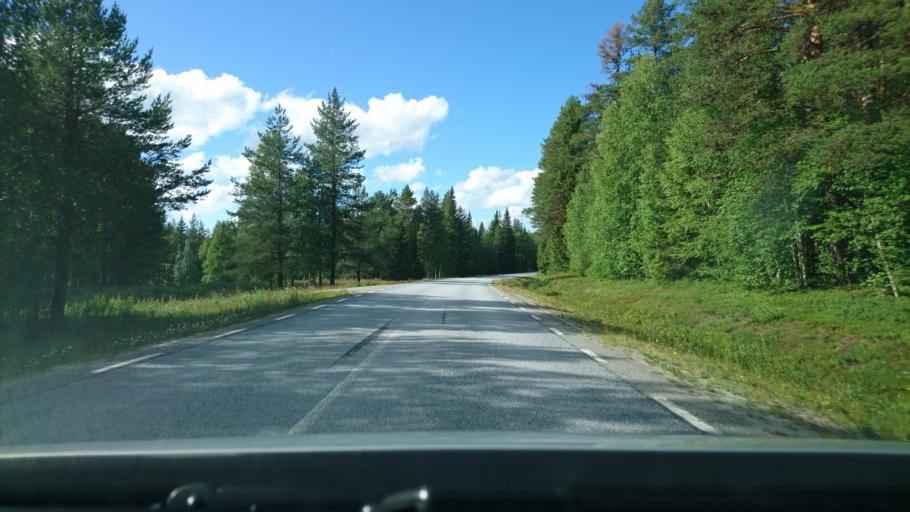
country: SE
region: Vaesterbotten
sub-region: Asele Kommun
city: Asele
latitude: 64.2133
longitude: 17.3136
